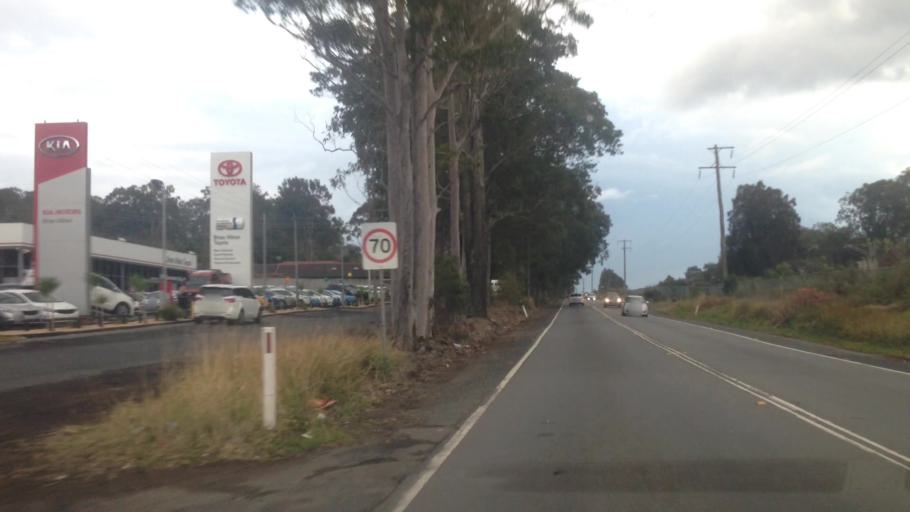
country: AU
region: New South Wales
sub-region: Wyong Shire
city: Jilliby
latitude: -33.2739
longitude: 151.4298
